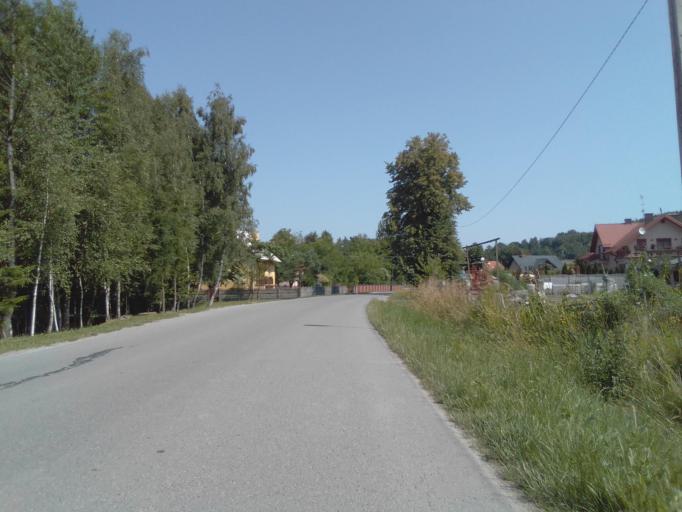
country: PL
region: Subcarpathian Voivodeship
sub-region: Powiat ropczycko-sedziszowski
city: Zagorzyce
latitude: 50.0376
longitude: 21.6559
